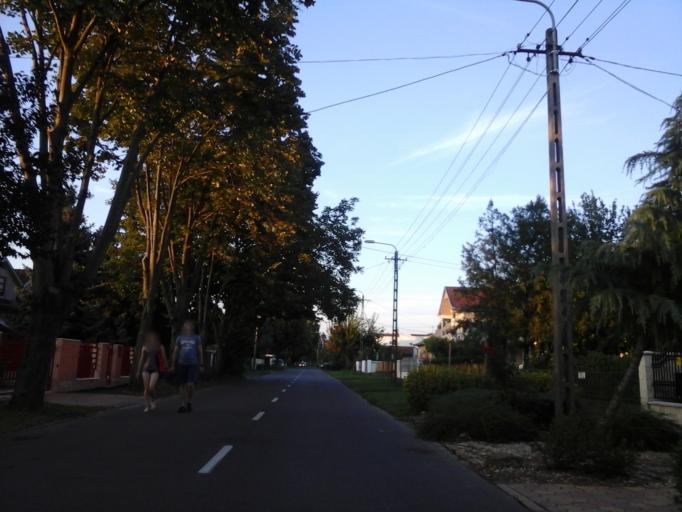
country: HU
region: Hajdu-Bihar
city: Hajduszoboszlo
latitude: 47.4574
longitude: 21.4097
